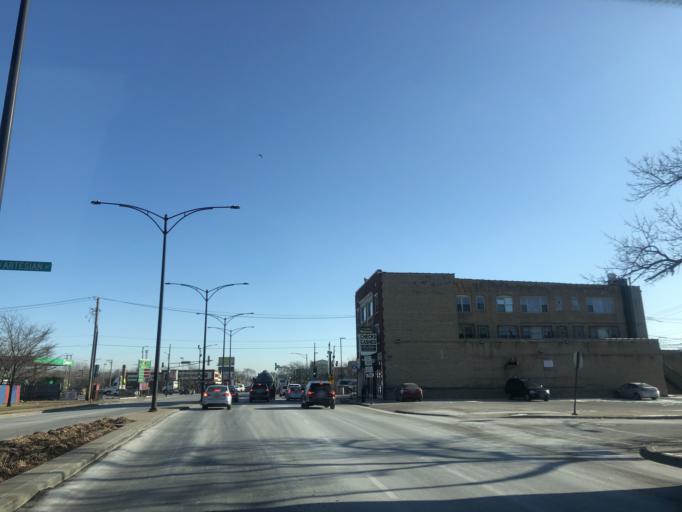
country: US
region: Illinois
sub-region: Cook County
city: Evergreen Park
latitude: 41.7501
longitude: -87.6844
